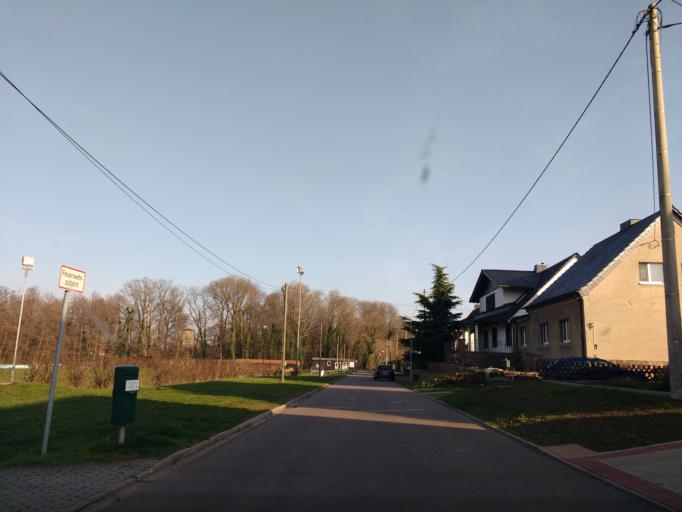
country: DE
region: Saxony-Anhalt
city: Oppin
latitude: 51.5514
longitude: 12.0279
